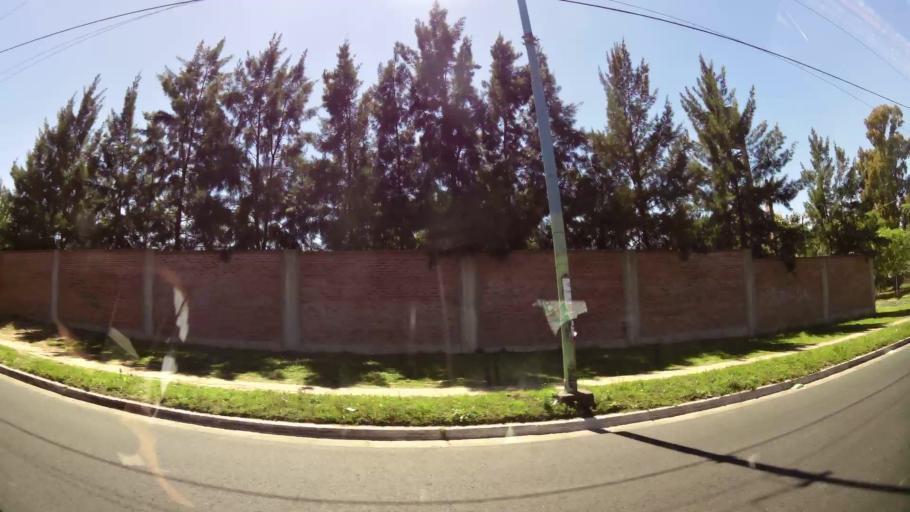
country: AR
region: Buenos Aires
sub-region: Partido de Quilmes
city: Quilmes
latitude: -34.7310
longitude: -58.2816
